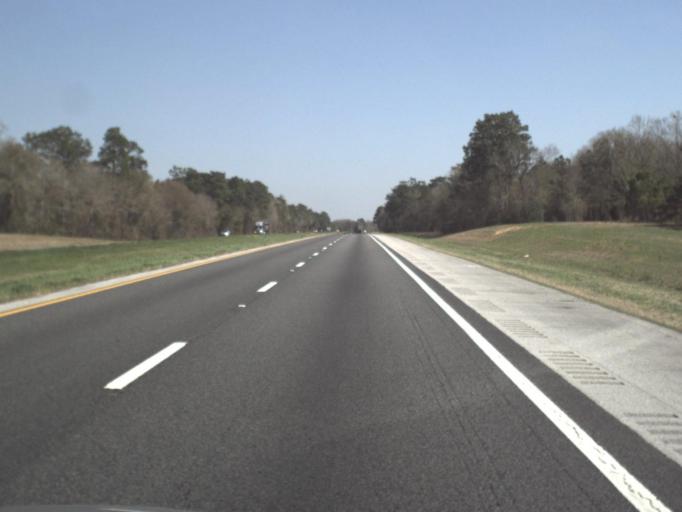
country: US
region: Florida
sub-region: Jackson County
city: Marianna
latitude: 30.6824
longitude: -85.0980
